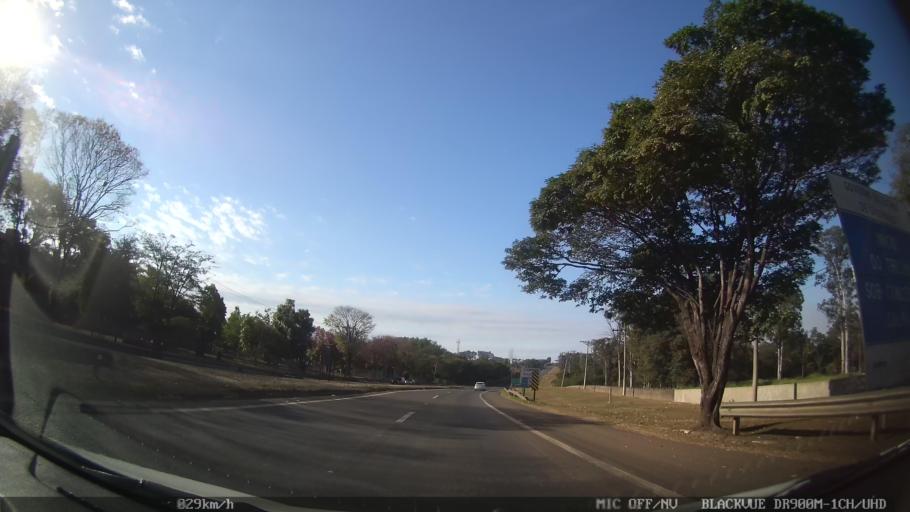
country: BR
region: Sao Paulo
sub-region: Piracicaba
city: Piracicaba
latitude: -22.6975
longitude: -47.6526
